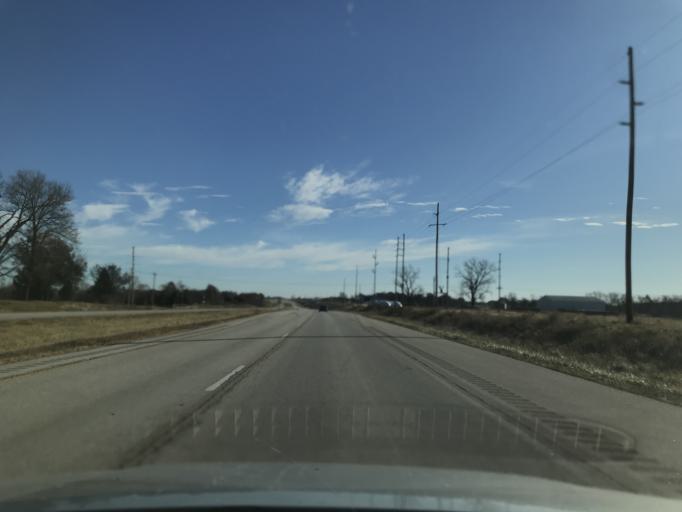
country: US
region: Illinois
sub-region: Hancock County
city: Carthage
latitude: 40.4154
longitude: -91.0843
